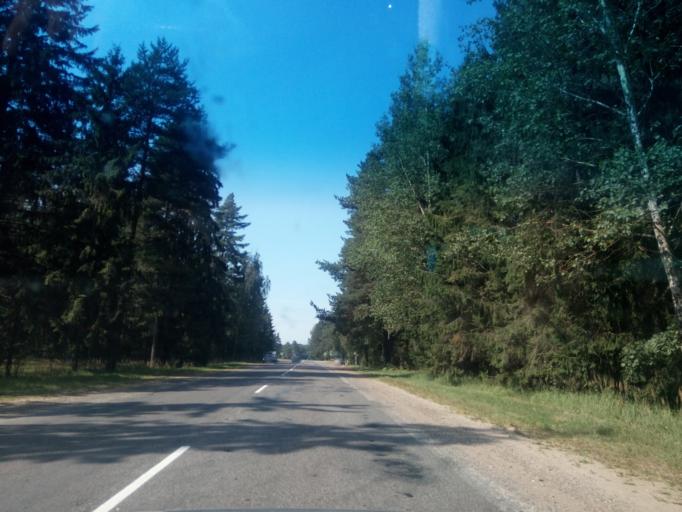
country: BY
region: Vitebsk
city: Vyerkhnyadzvinsk
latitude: 55.7973
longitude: 27.9563
